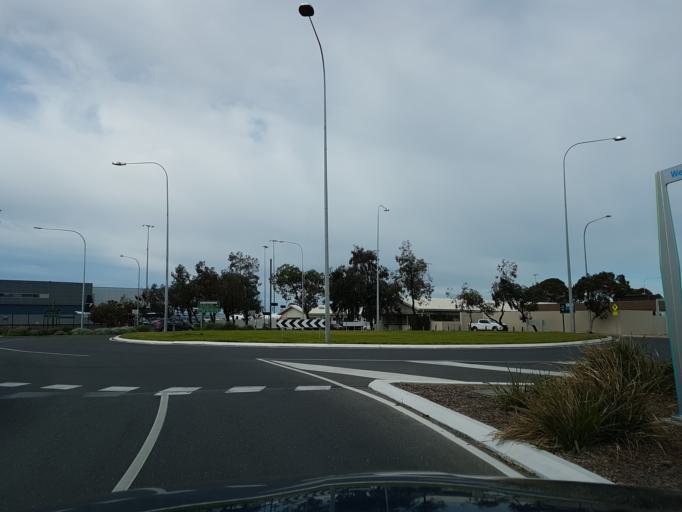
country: AU
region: South Australia
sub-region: City of West Torrens
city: Plympton
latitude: -34.9391
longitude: 138.5342
